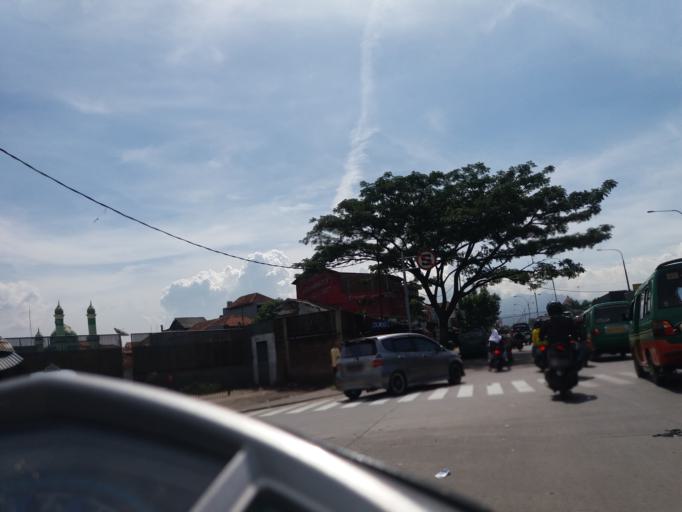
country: ID
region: West Java
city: Margahayukencana
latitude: -6.9305
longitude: 107.5759
